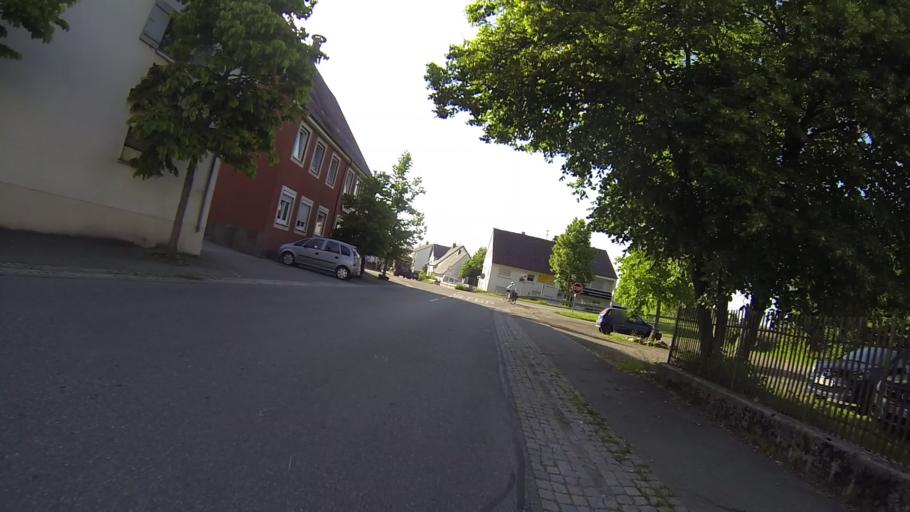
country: DE
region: Baden-Wuerttemberg
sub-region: Tuebingen Region
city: Maselheim
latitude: 48.1577
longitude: 9.8567
